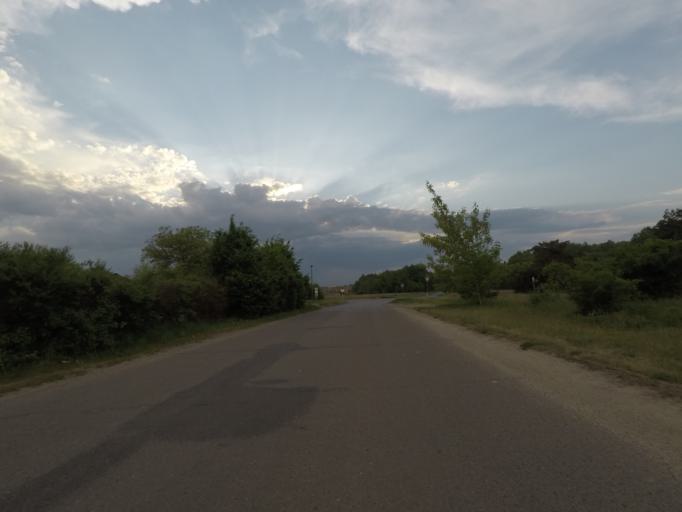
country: DE
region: Brandenburg
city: Eberswalde
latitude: 52.8462
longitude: 13.7468
